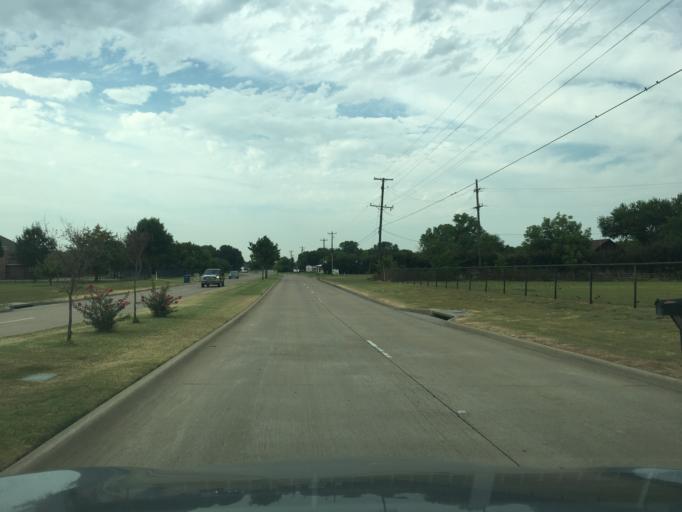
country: US
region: Texas
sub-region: Collin County
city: Parker
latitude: 33.0461
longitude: -96.5947
